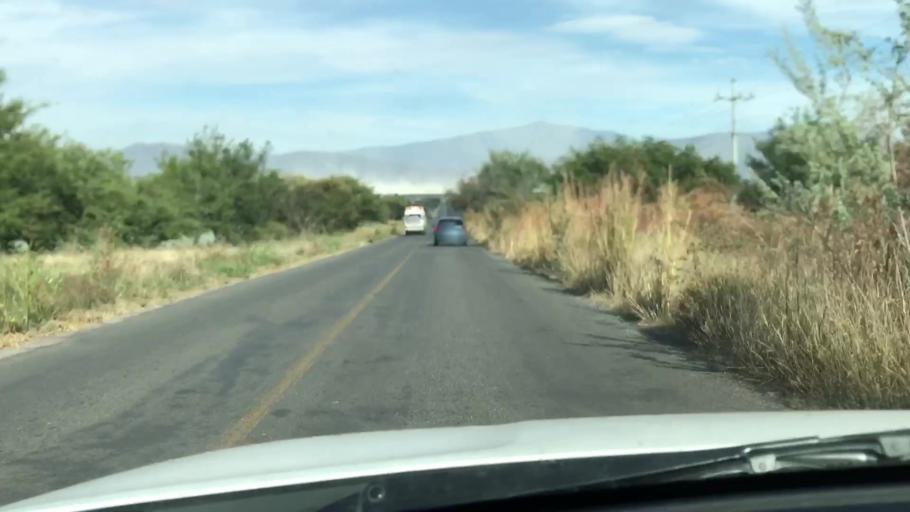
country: MX
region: Jalisco
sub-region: Zacoalco de Torres
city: Barranca de Otates (Barranca de Otatan)
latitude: 20.2752
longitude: -103.6309
